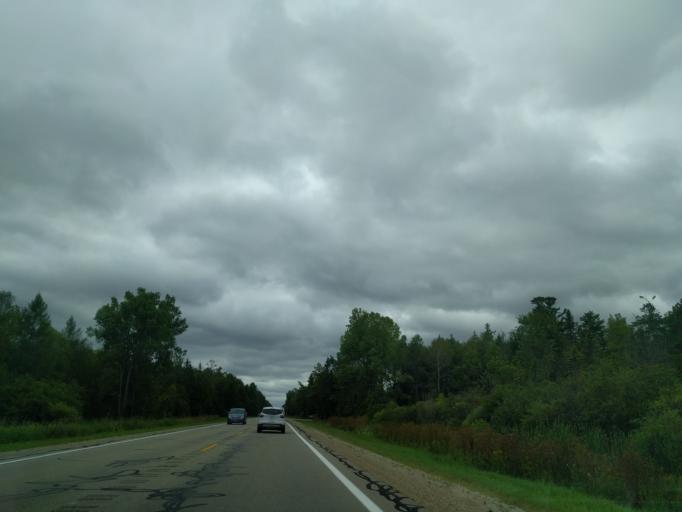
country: US
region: Michigan
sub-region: Menominee County
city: Menominee
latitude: 45.3522
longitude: -87.4048
